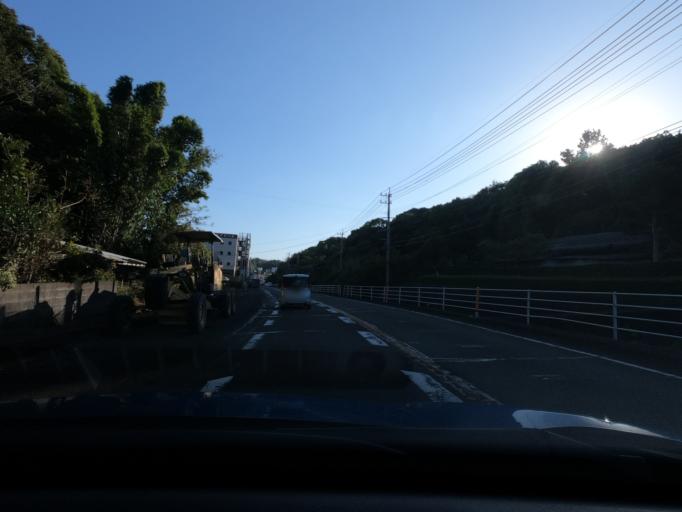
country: JP
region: Kagoshima
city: Akune
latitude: 32.0451
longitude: 130.2162
